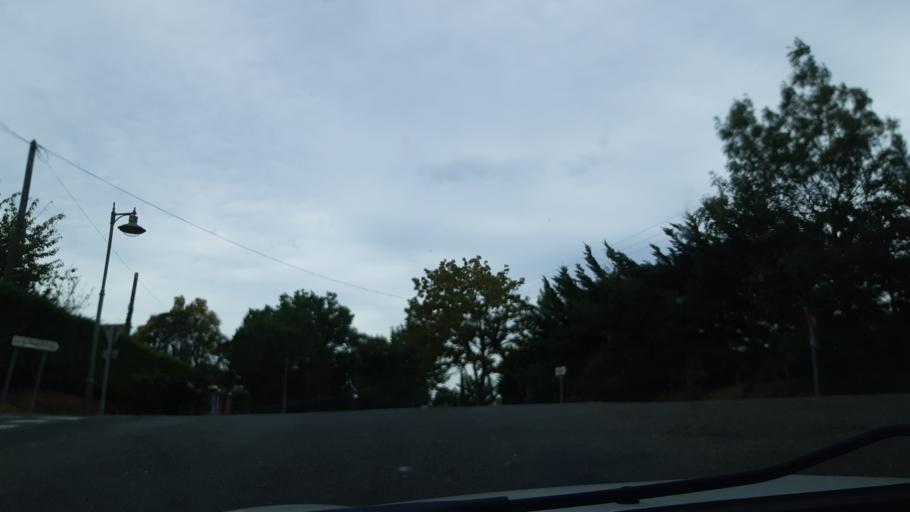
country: FR
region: Midi-Pyrenees
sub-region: Departement du Gers
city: Gimont
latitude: 43.6786
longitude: 0.9939
